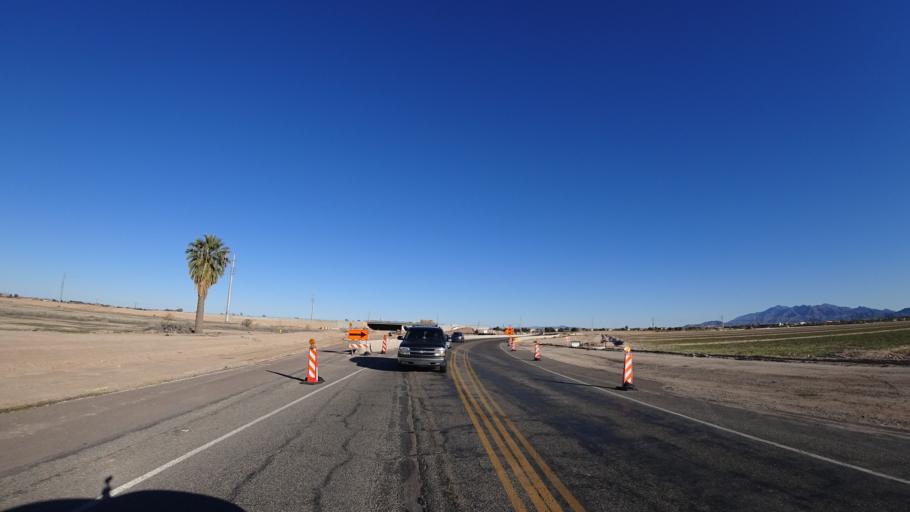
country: US
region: Arizona
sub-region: Maricopa County
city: Goodyear
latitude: 33.4502
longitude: -112.4303
